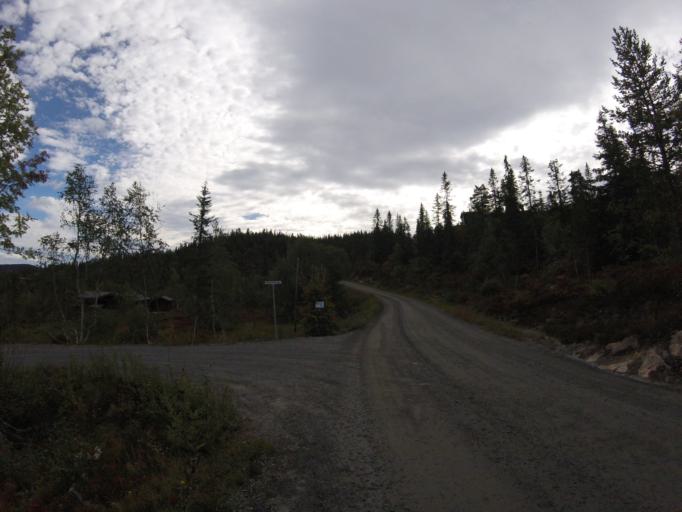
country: NO
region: Buskerud
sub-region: Flesberg
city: Lampeland
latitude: 59.7695
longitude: 9.4522
